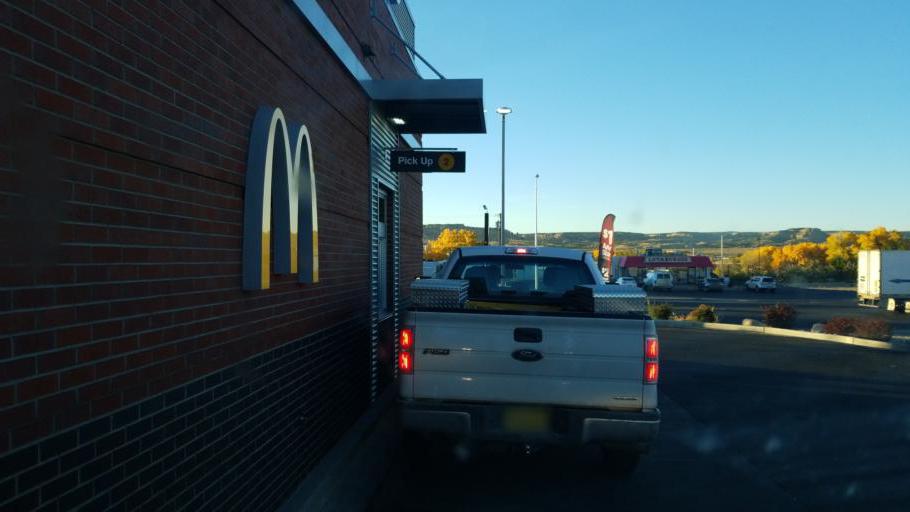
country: US
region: New Mexico
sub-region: San Juan County
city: Farmington
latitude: 36.7320
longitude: -108.2316
